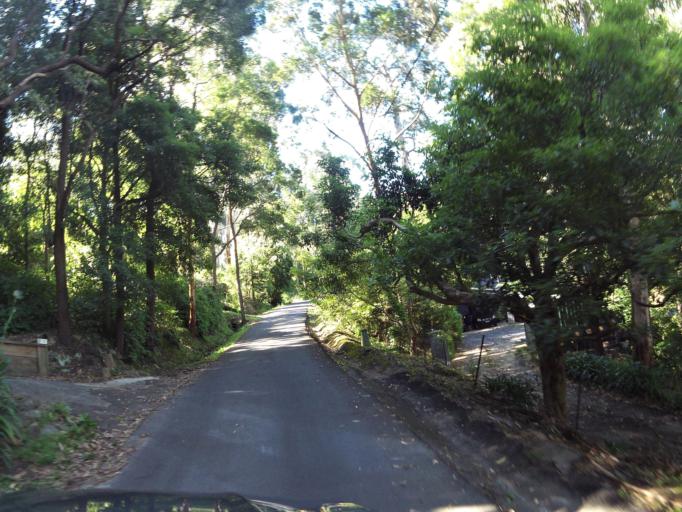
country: AU
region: Victoria
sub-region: Yarra Ranges
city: Tremont
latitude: -37.8973
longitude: 145.3397
